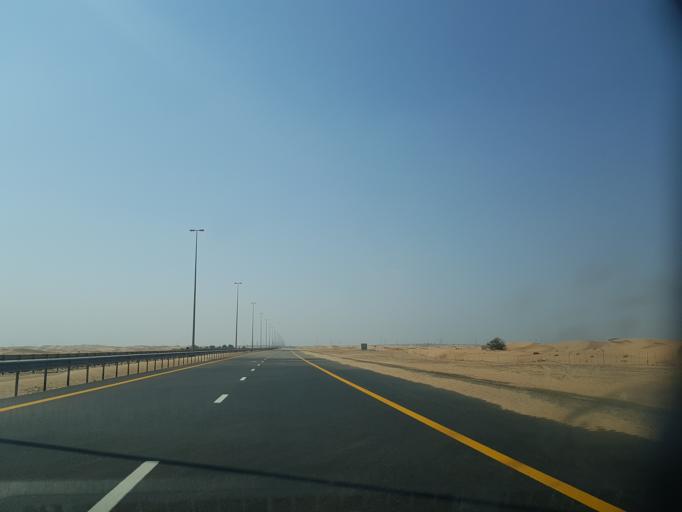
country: AE
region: Ash Shariqah
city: Sharjah
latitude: 25.2739
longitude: 55.6231
